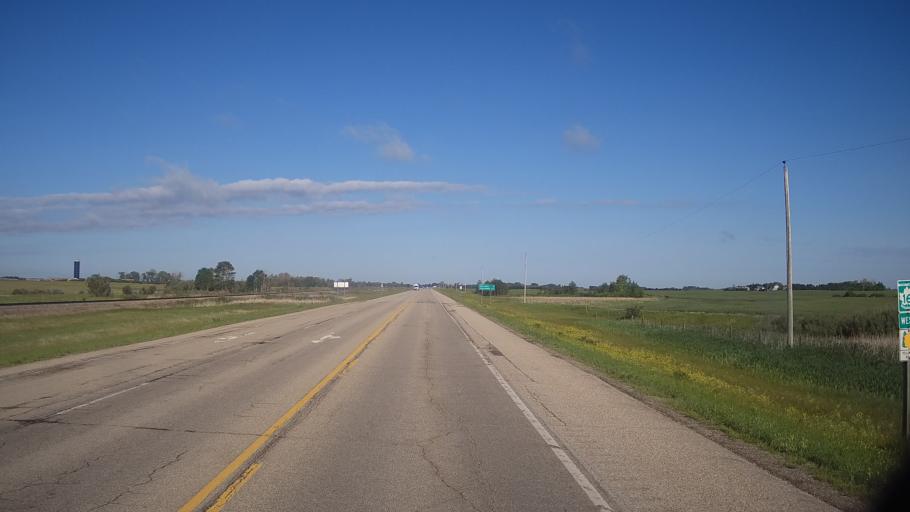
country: CA
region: Saskatchewan
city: Lanigan
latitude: 51.8666
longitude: -105.1478
